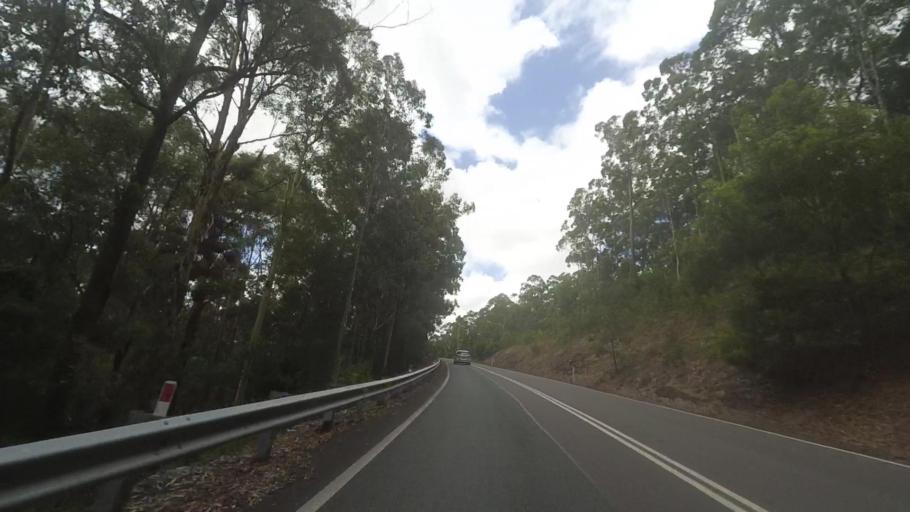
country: AU
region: New South Wales
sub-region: Great Lakes
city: Bulahdelah
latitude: -32.3942
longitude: 152.2464
